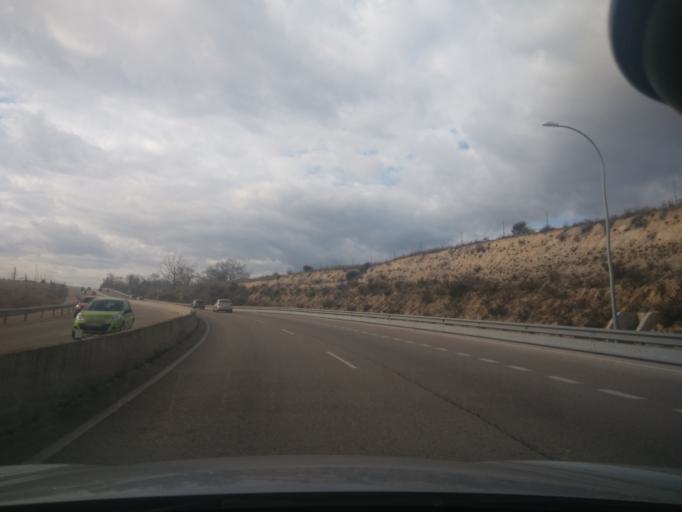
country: ES
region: Madrid
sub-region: Provincia de Madrid
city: Alcobendas
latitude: 40.5498
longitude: -3.6638
